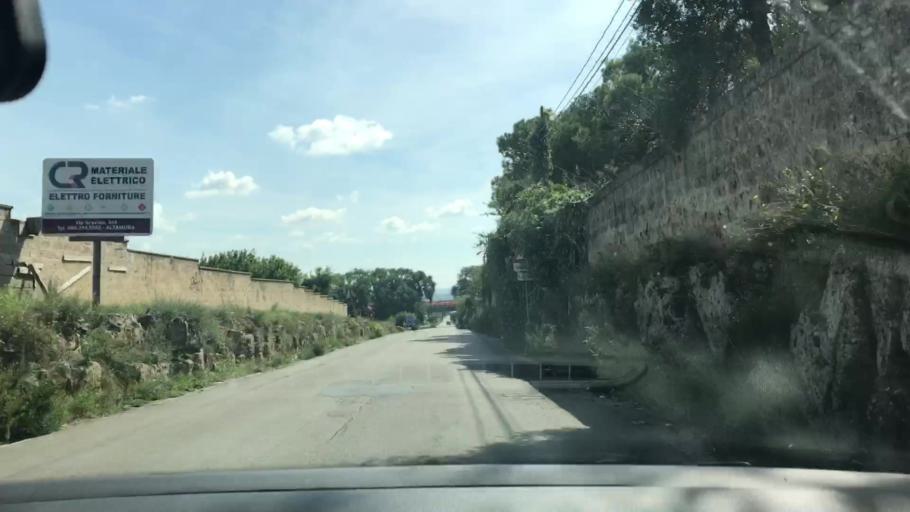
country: IT
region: Apulia
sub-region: Provincia di Bari
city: Altamura
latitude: 40.8250
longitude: 16.5675
